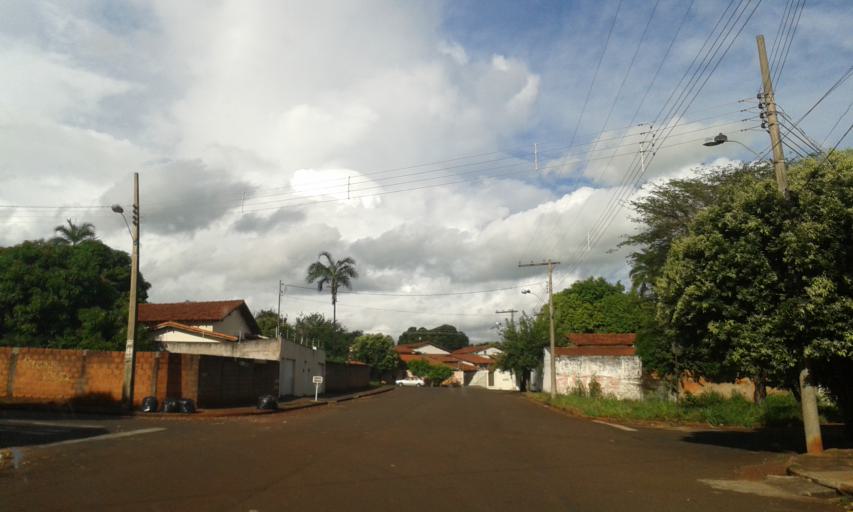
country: BR
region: Minas Gerais
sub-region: Ituiutaba
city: Ituiutaba
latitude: -18.9711
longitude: -49.4526
